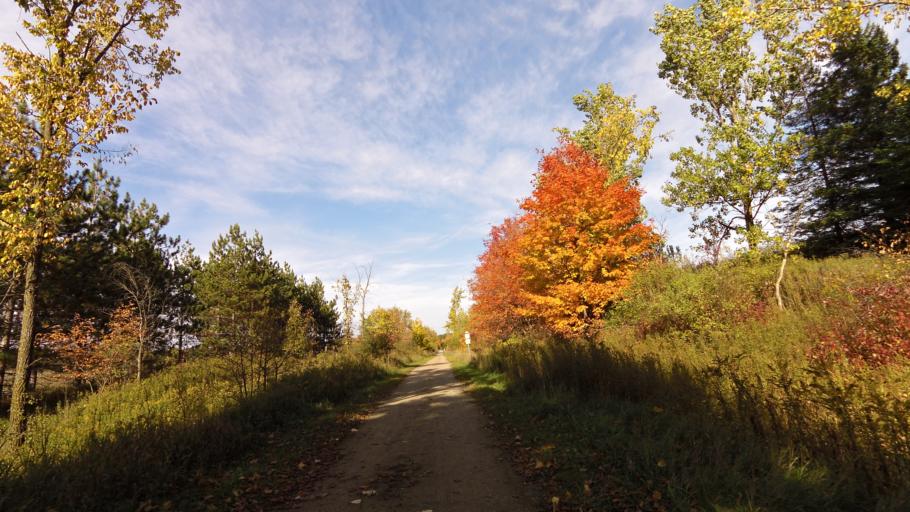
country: CA
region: Ontario
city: Orangeville
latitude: 43.8101
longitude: -80.0305
